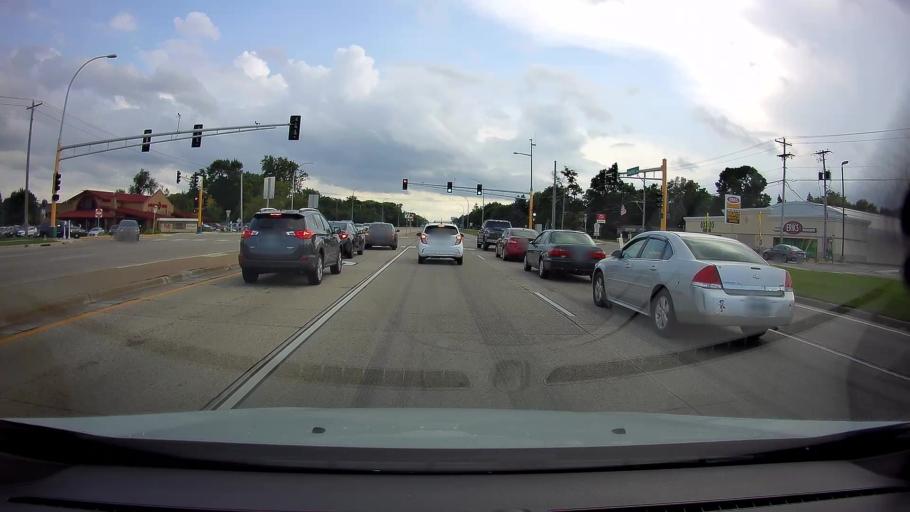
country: US
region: Minnesota
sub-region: Ramsey County
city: Roseville
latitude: 45.0037
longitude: -93.1665
